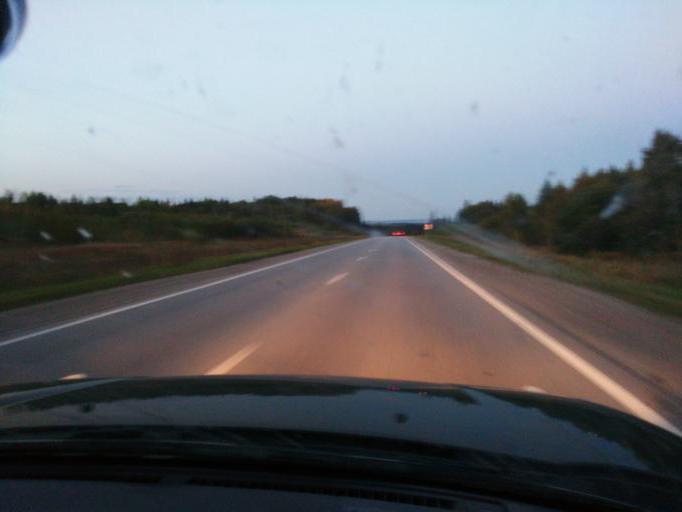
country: RU
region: Perm
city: Kalino
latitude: 58.2719
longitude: 57.3773
